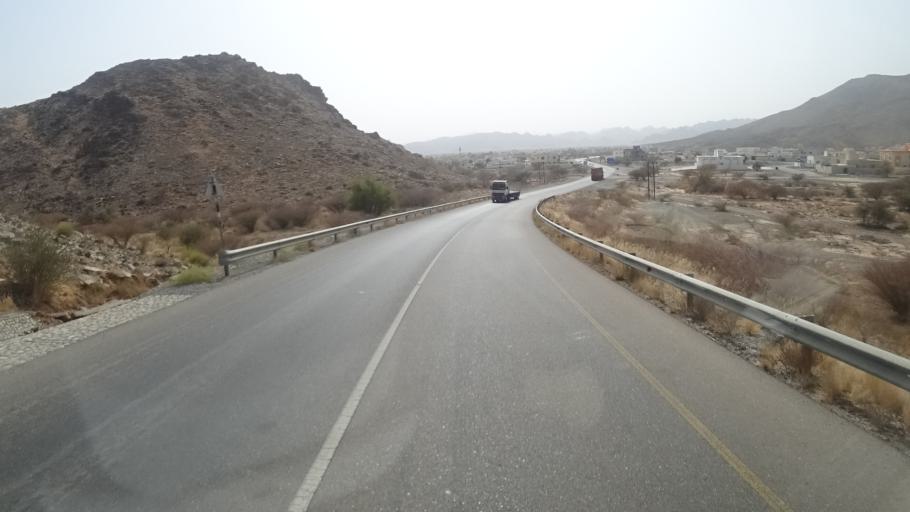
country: OM
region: Muhafazat ad Dakhiliyah
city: Nizwa
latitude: 23.0033
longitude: 57.5665
